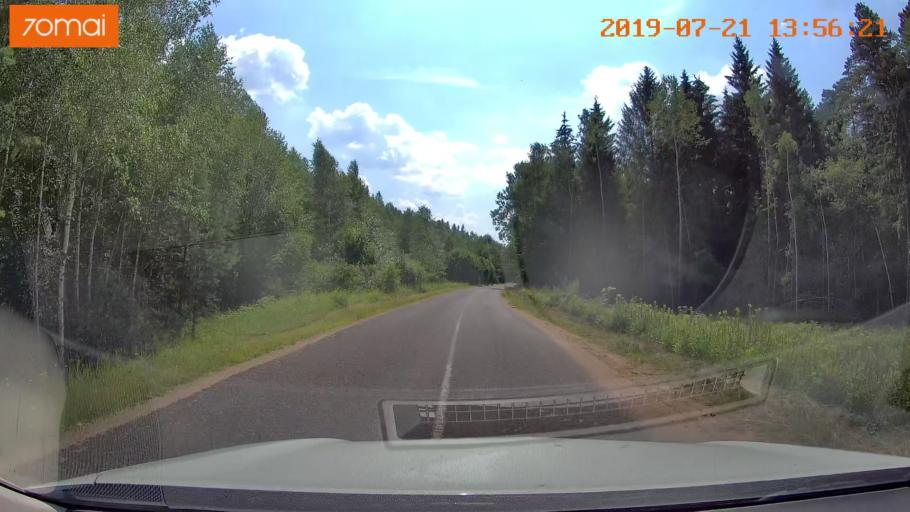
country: BY
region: Grodnenskaya
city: Lyubcha
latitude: 53.7803
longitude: 26.1000
